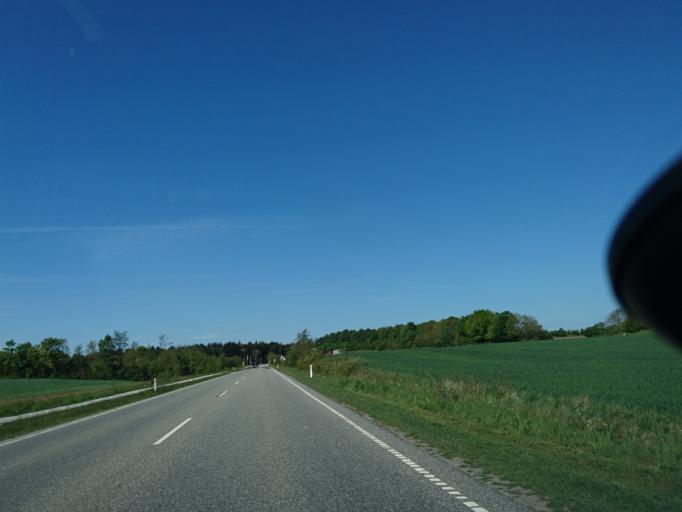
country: DK
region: North Denmark
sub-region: Hjorring Kommune
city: Sindal
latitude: 57.4708
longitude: 10.2254
